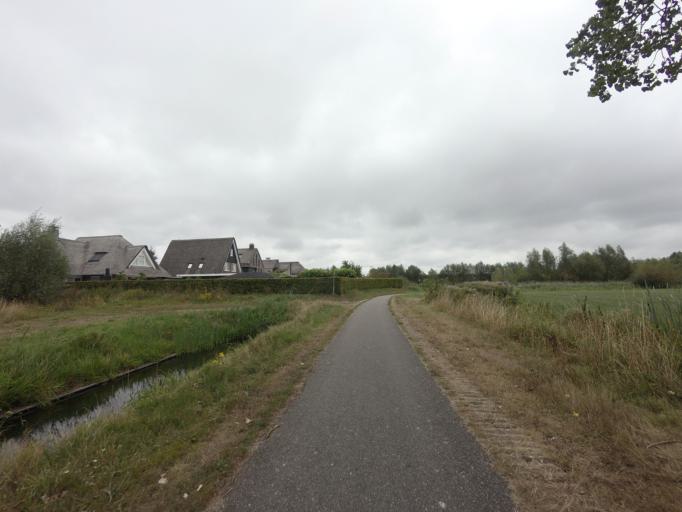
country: NL
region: Gelderland
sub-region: Gemeente Overbetuwe
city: Driel
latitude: 51.9588
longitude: 5.8305
